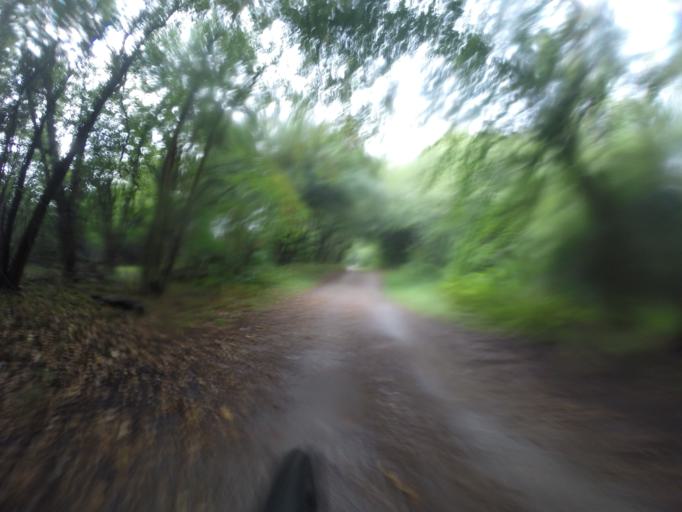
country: DK
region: Capital Region
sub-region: Herlev Kommune
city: Herlev
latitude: 55.7533
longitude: 12.4301
